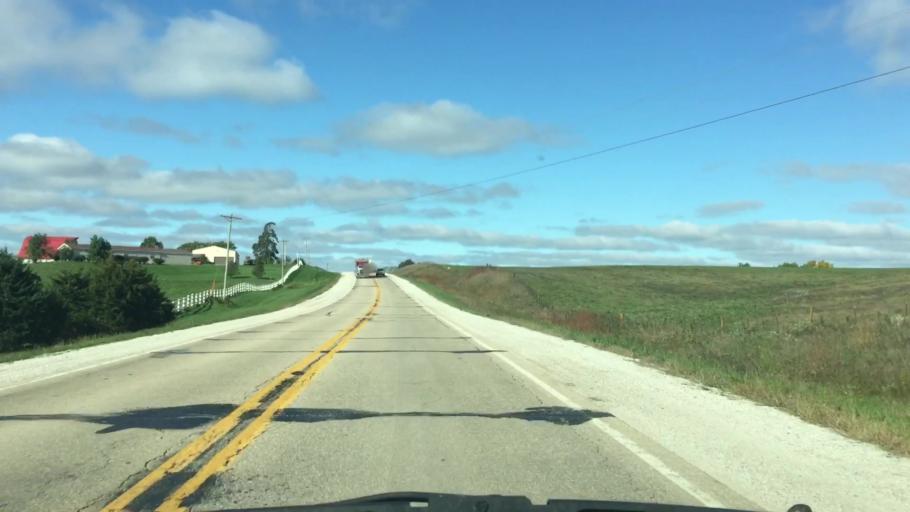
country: US
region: Iowa
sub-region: Decatur County
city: Leon
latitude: 40.7418
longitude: -93.7963
